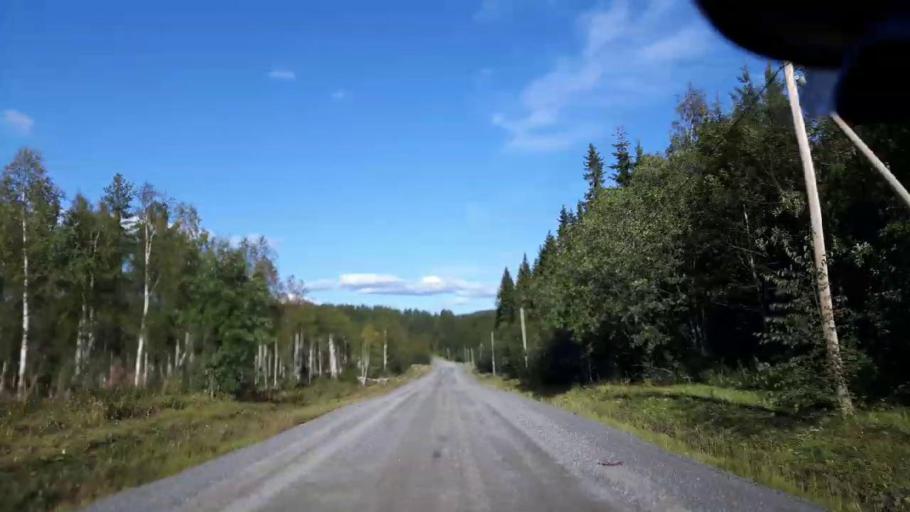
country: SE
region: Vaesternorrland
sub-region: Solleftea Kommun
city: As
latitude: 63.4558
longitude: 16.2425
